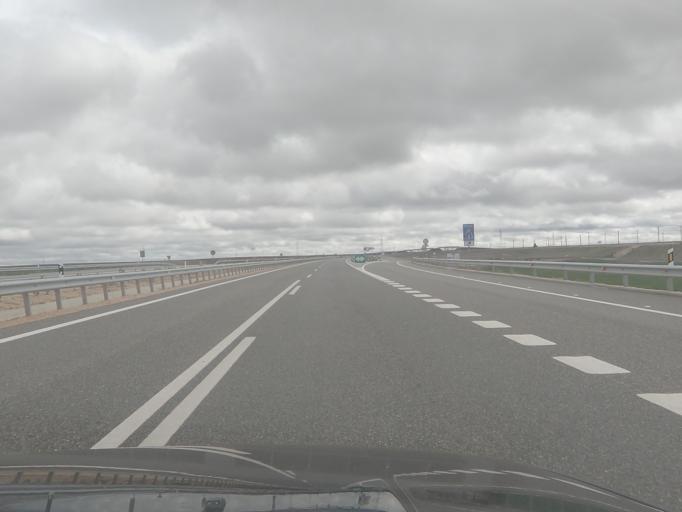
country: ES
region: Castille and Leon
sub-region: Provincia de Zamora
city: Montamarta
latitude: 41.6363
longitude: -5.7906
